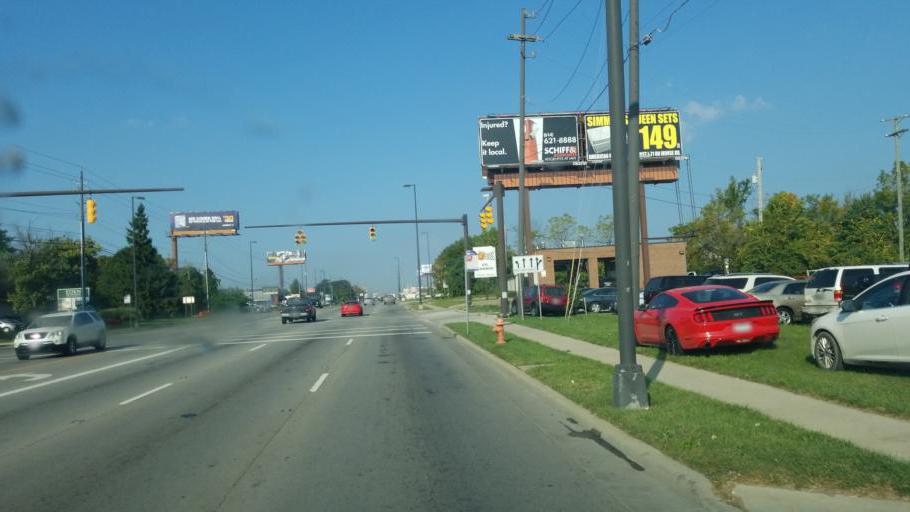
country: US
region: Ohio
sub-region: Franklin County
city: Minerva Park
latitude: 40.0592
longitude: -82.9441
